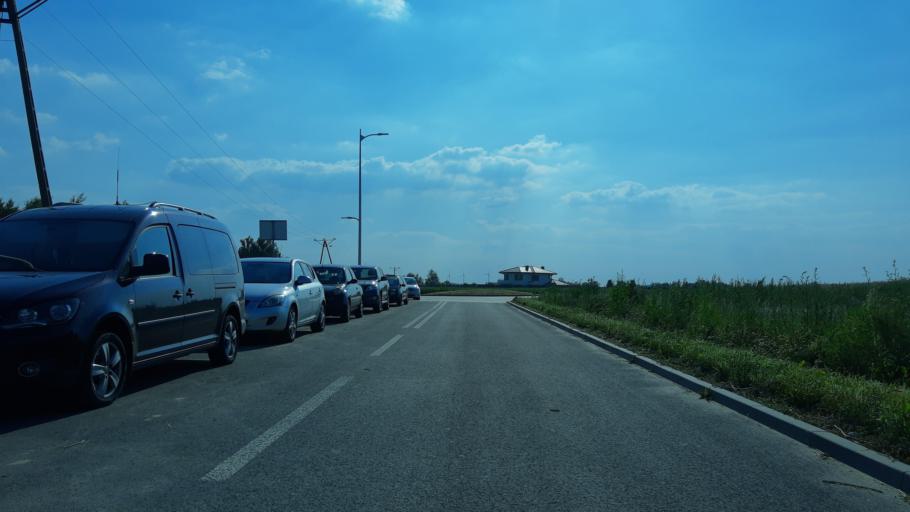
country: PL
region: Lodz Voivodeship
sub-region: Powiat sieradzki
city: Sieradz
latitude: 51.5855
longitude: 18.7061
